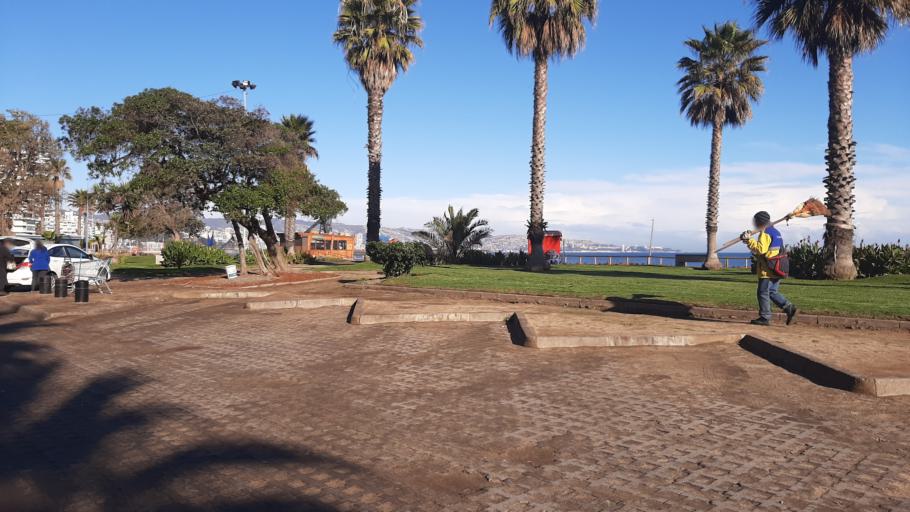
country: CL
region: Valparaiso
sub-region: Provincia de Valparaiso
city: Vina del Mar
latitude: -33.0097
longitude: -71.5520
